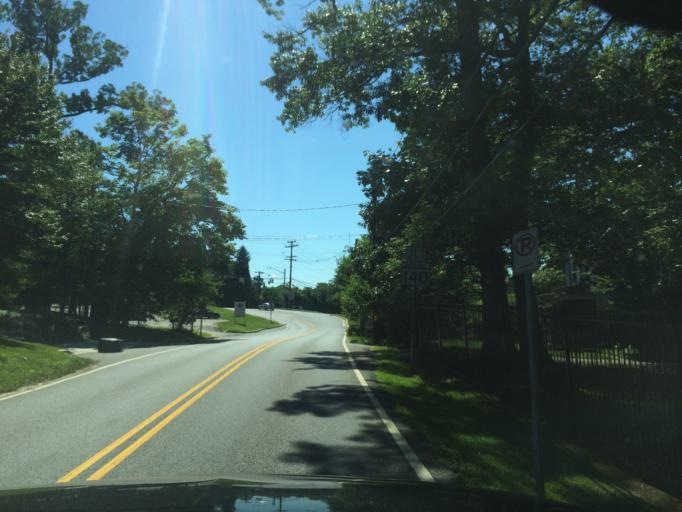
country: US
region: Maryland
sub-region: Baltimore County
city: Garrison
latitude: 39.4040
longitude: -76.7555
